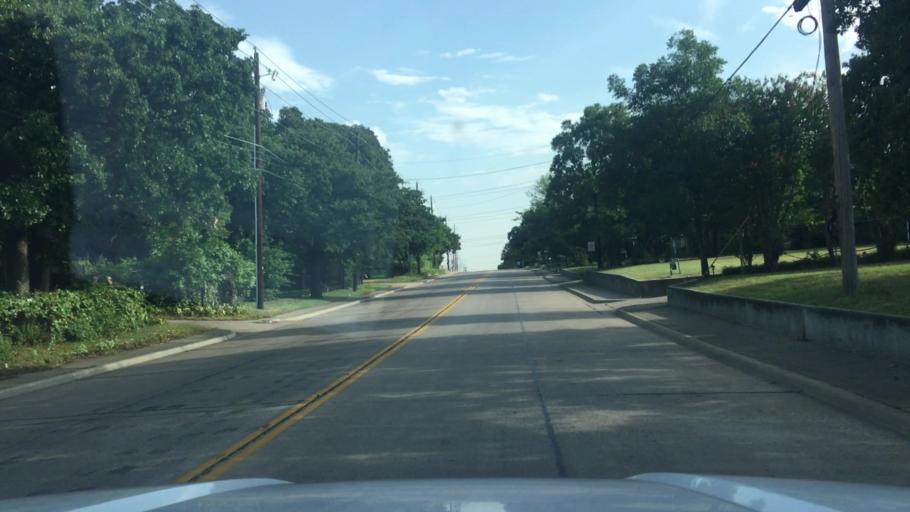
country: US
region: Texas
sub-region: Dallas County
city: Irving
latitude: 32.8106
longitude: -96.9169
